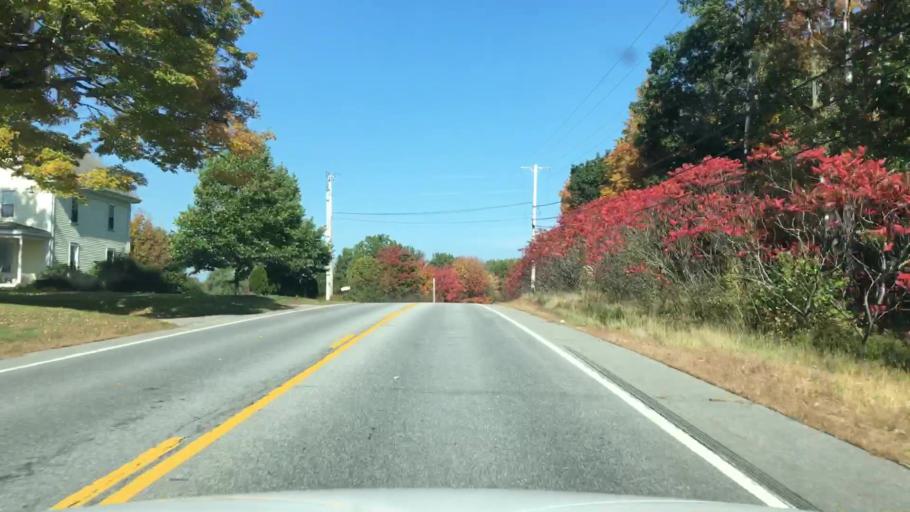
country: US
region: Maine
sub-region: Sagadahoc County
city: Topsham
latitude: 43.9771
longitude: -69.9602
